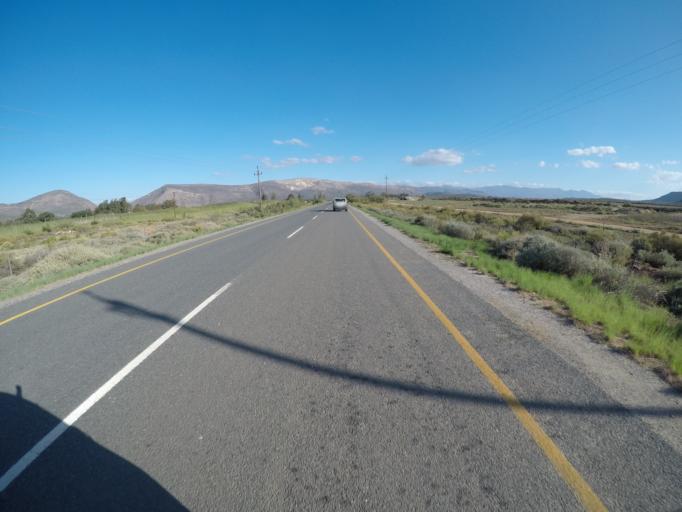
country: ZA
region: Western Cape
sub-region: Cape Winelands District Municipality
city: Ashton
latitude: -33.8035
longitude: 19.7818
